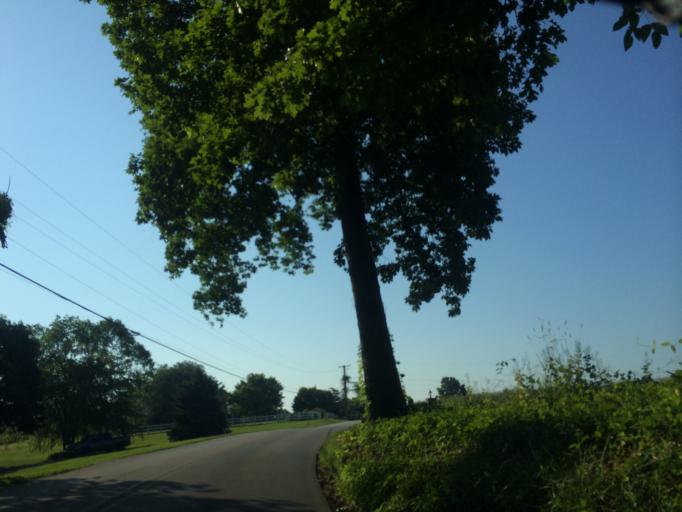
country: US
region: Maryland
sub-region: Howard County
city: Highland
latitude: 39.2171
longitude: -76.9798
